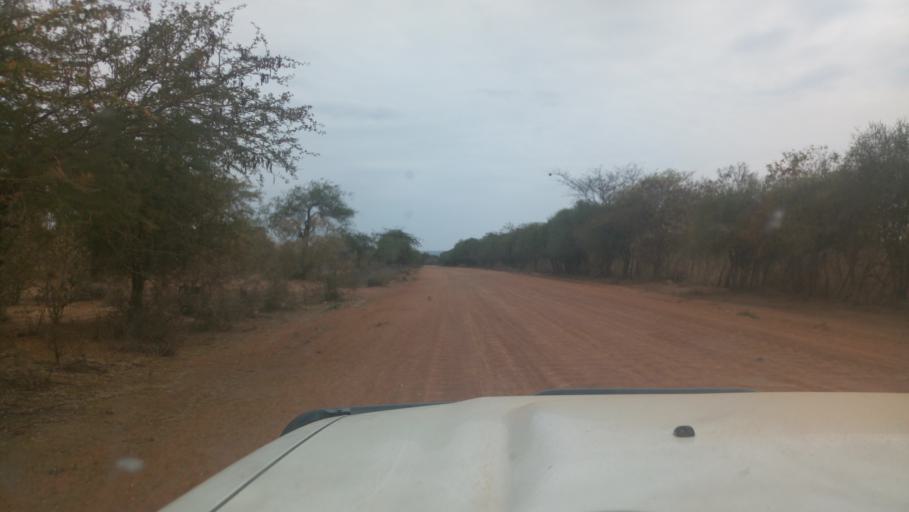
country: KE
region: Kitui
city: Kitui
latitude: -1.6341
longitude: 37.9090
